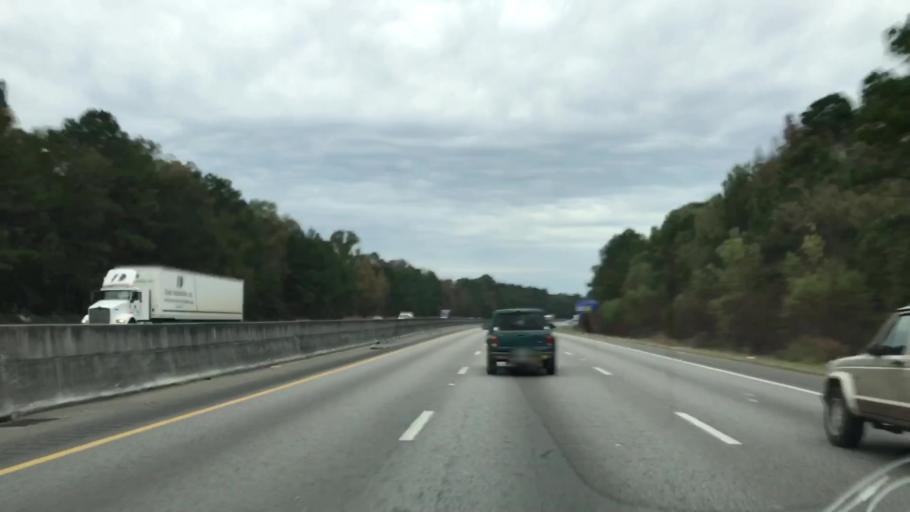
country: US
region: South Carolina
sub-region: Berkeley County
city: Goose Creek
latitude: 32.9593
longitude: -80.0698
